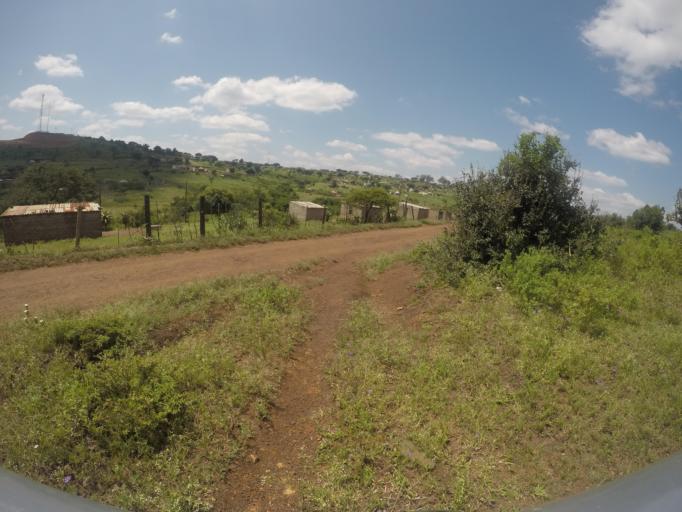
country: ZA
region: KwaZulu-Natal
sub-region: uThungulu District Municipality
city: Empangeni
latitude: -28.6012
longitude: 31.7360
